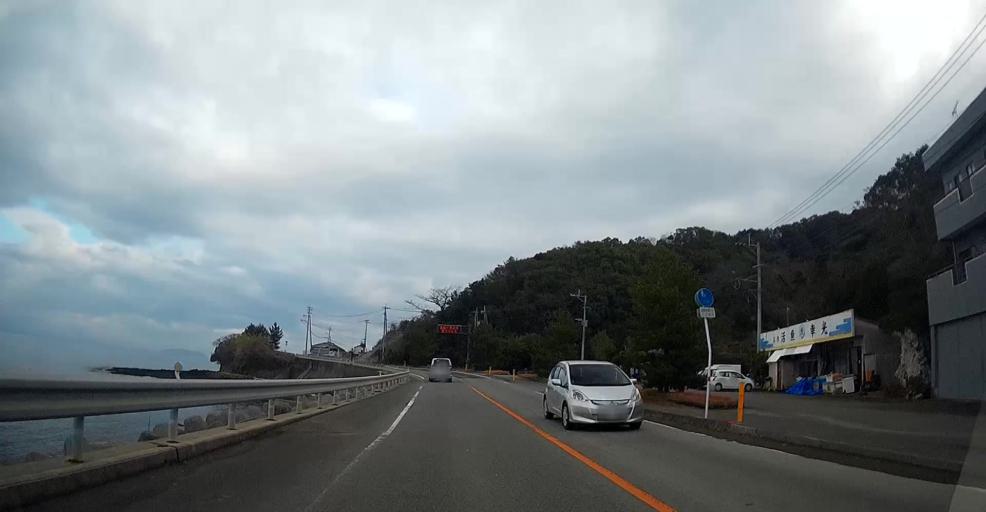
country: JP
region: Kumamoto
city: Hondo
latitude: 32.4853
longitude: 130.2837
